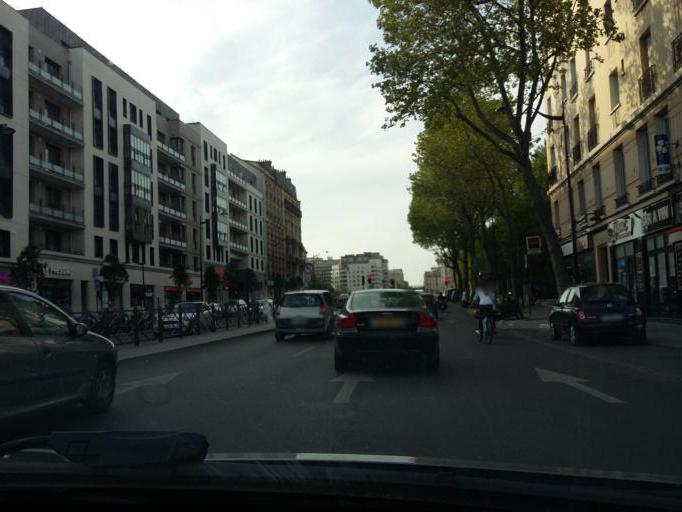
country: FR
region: Ile-de-France
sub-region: Departement des Hauts-de-Seine
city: Neuilly-sur-Seine
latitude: 48.8943
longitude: 2.2669
